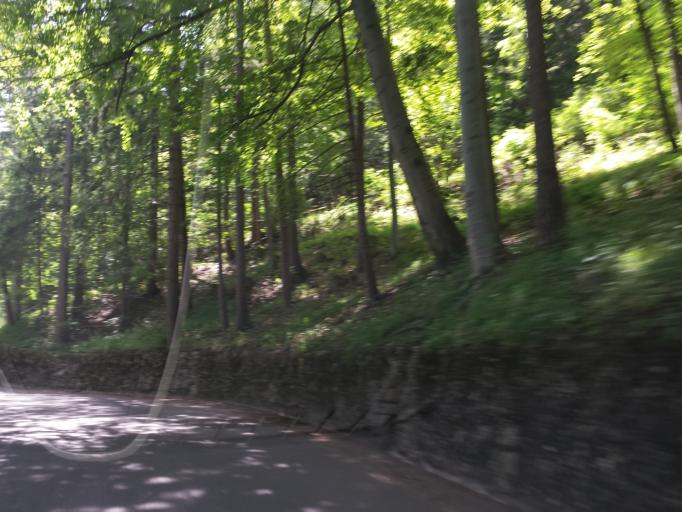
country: AT
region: Lower Austria
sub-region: Politischer Bezirk Neunkirchen
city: Semmering
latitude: 47.6441
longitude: 15.8281
